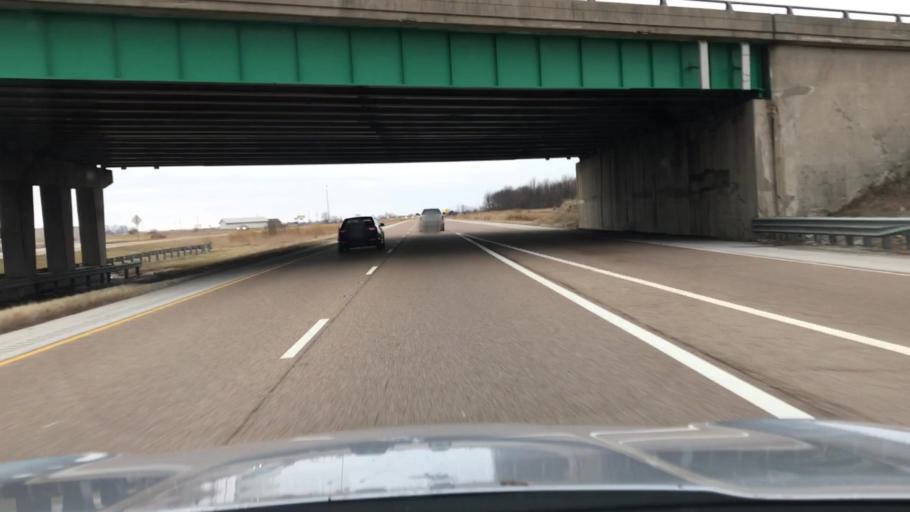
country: US
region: Illinois
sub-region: Montgomery County
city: Litchfield
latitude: 39.1756
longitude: -89.6812
